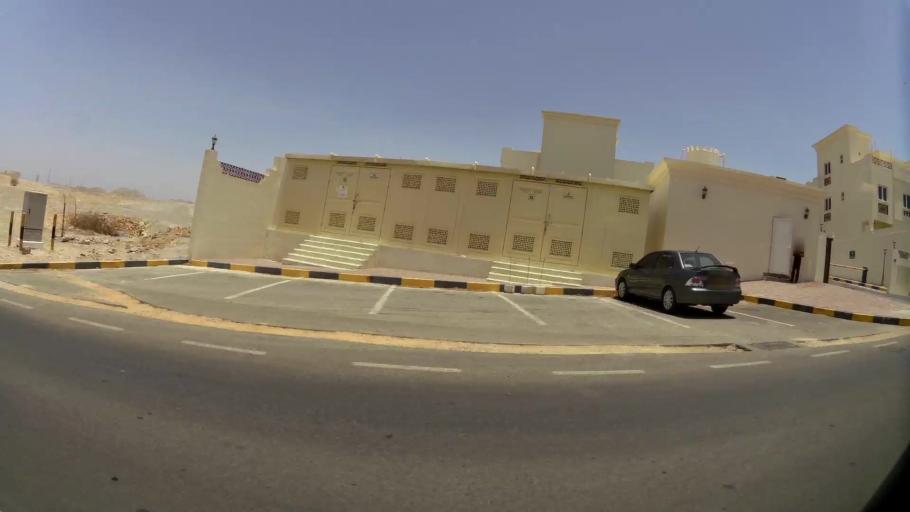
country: OM
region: Muhafazat Masqat
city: Bawshar
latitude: 23.6041
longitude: 58.4865
